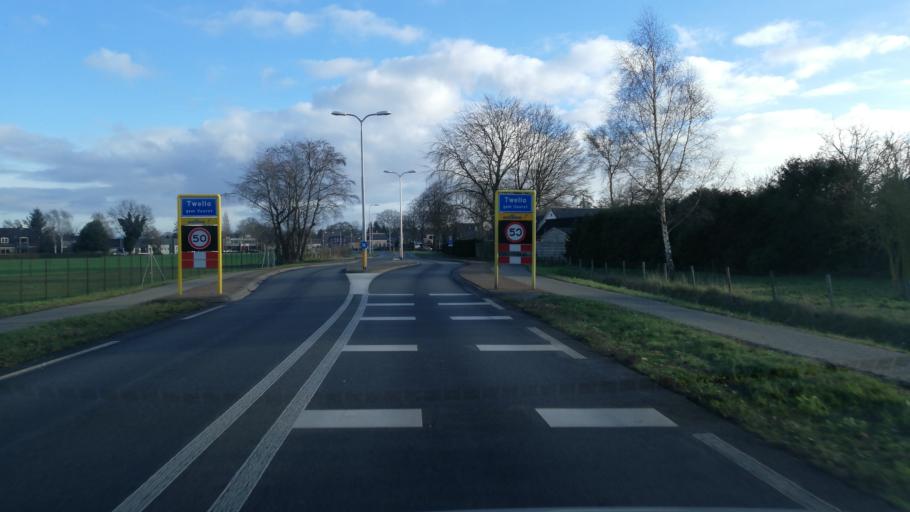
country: NL
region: Gelderland
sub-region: Gemeente Voorst
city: Twello
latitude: 52.2396
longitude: 6.0922
